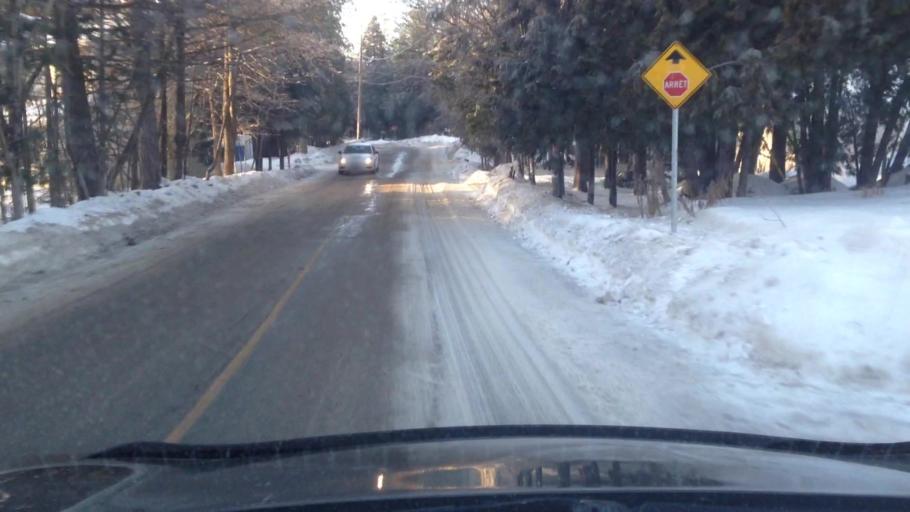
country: CA
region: Quebec
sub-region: Lanaudiere
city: Sainte-Julienne
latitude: 45.9459
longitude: -73.7437
